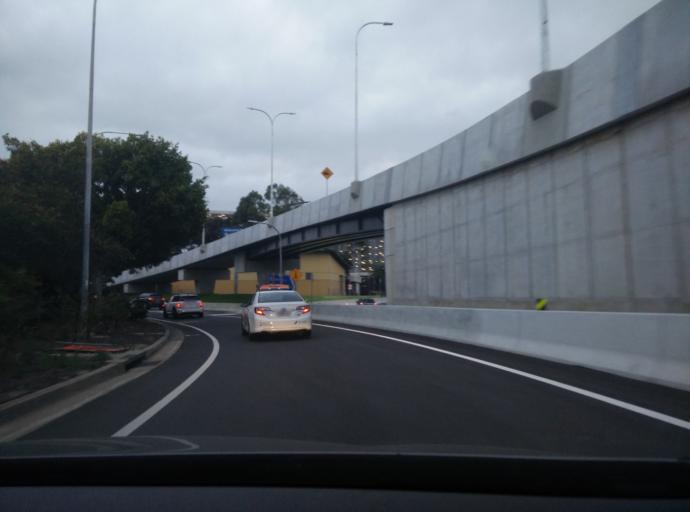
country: AU
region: New South Wales
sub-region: Rockdale
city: Arncliffe
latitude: -33.9318
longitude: 151.1639
